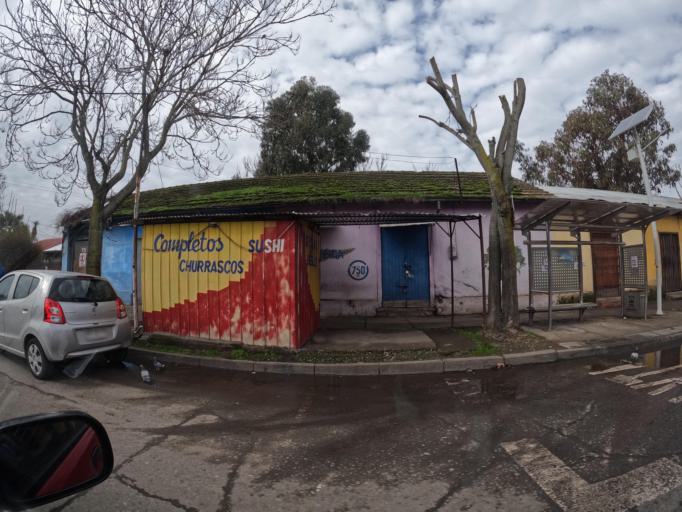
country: CL
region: Maule
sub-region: Provincia de Linares
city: Linares
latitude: -35.8442
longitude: -71.5901
